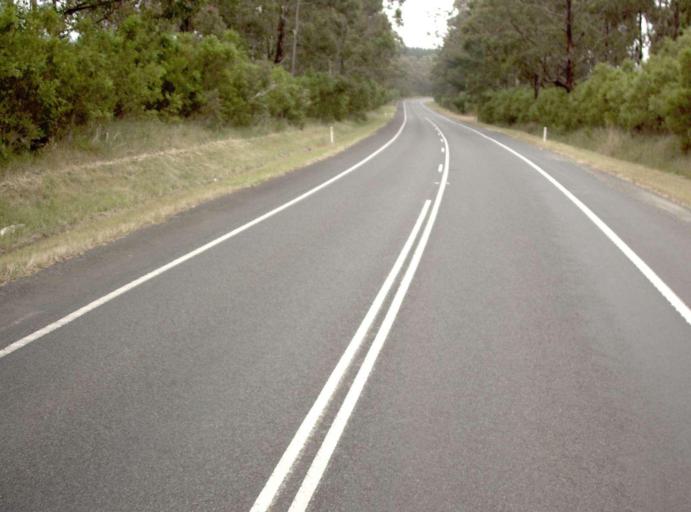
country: AU
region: Victoria
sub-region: Latrobe
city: Moe
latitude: -38.3044
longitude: 146.2788
